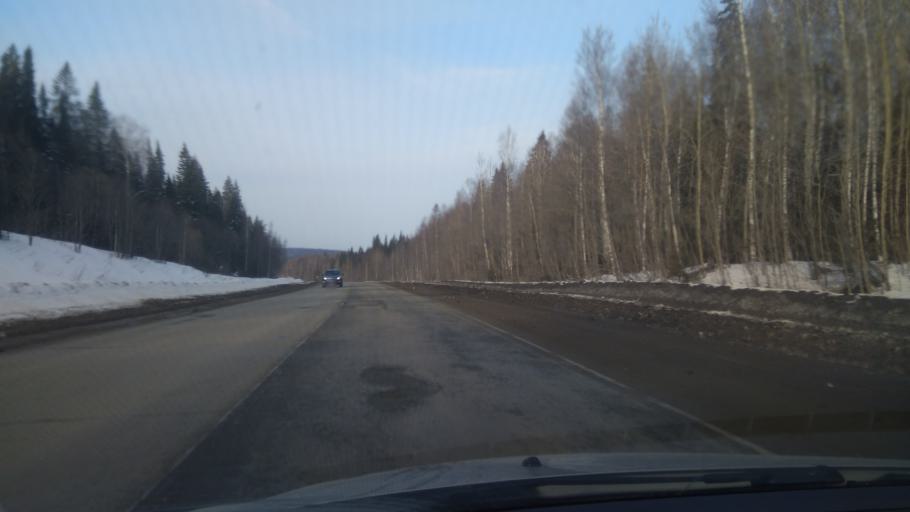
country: RU
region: Sverdlovsk
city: Bisert'
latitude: 56.8275
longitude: 59.2057
